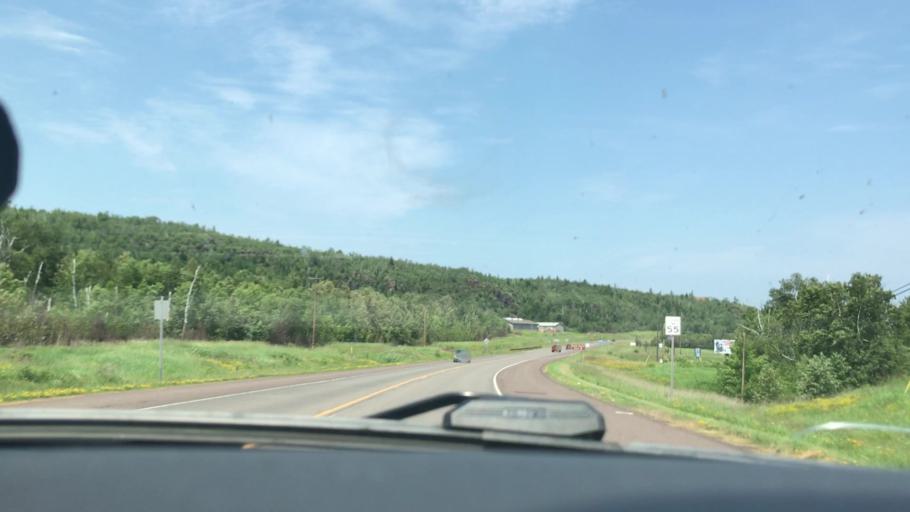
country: US
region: Minnesota
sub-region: Lake County
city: Silver Bay
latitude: 47.2976
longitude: -91.2553
